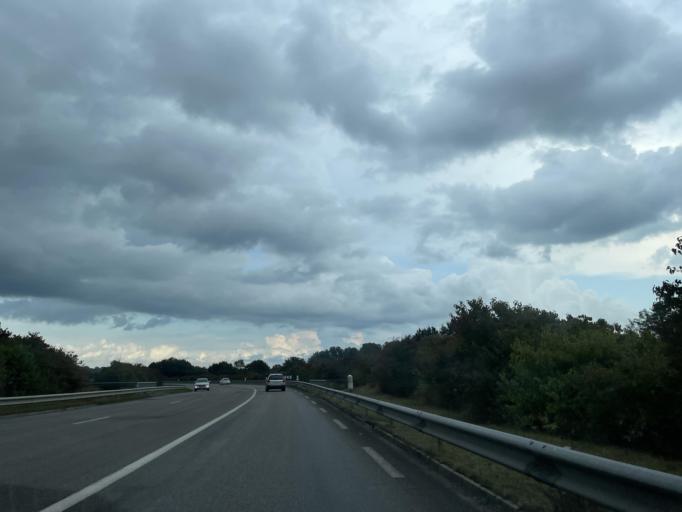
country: FR
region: Haute-Normandie
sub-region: Departement de la Seine-Maritime
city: Forges-les-Eaux
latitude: 49.6008
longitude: 1.5586
